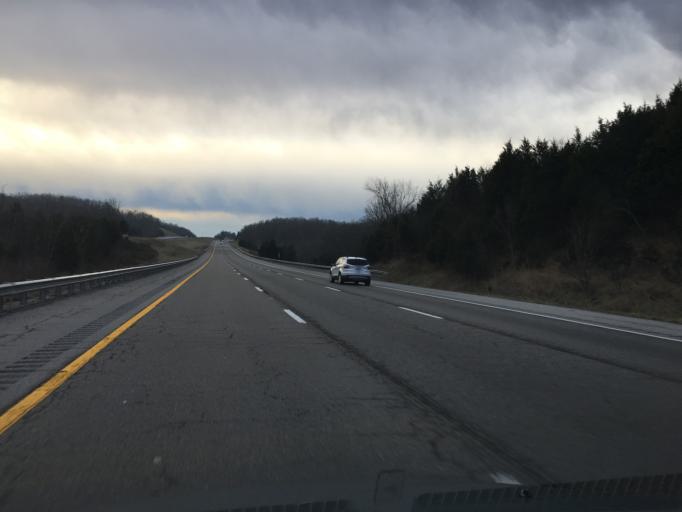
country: US
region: Kentucky
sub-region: Grant County
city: Williamstown
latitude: 38.4720
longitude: -84.5802
